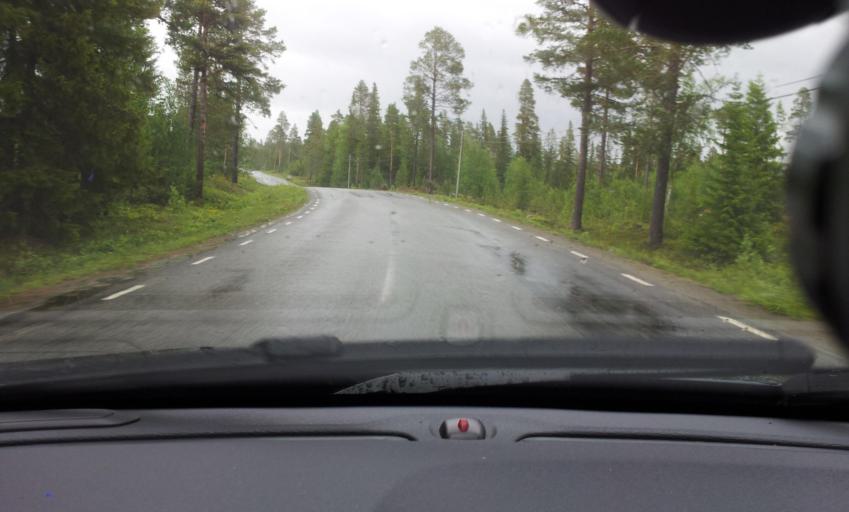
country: SE
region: Jaemtland
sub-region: Are Kommun
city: Are
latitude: 63.1855
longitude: 13.1263
